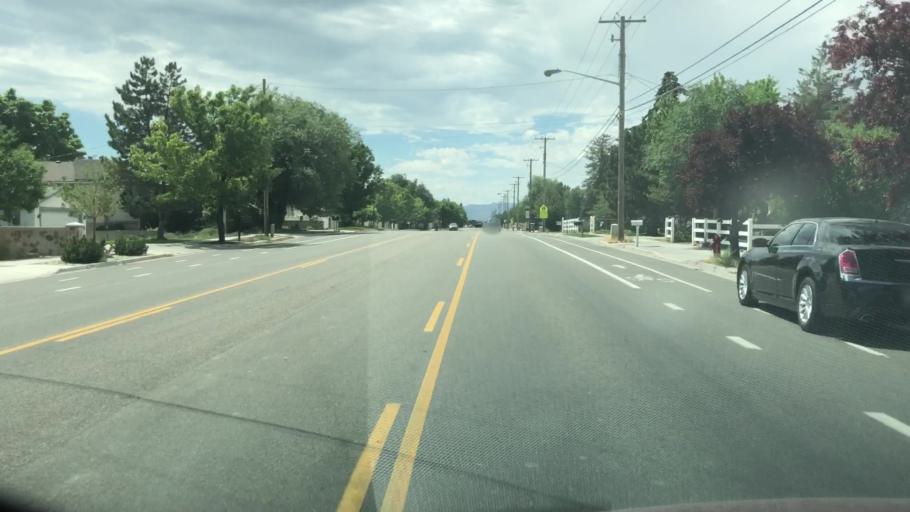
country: US
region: Utah
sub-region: Salt Lake County
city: South Jordan
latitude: 40.5504
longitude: -111.9292
